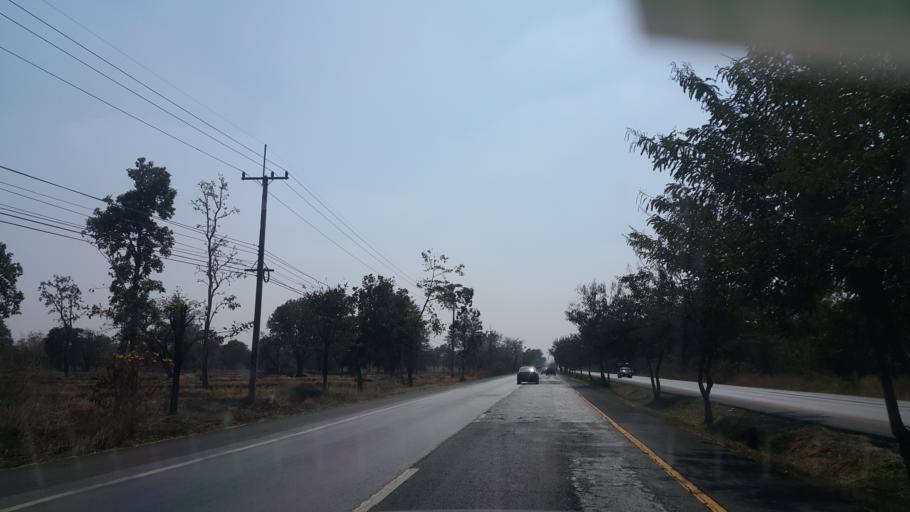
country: TH
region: Nakhon Ratchasima
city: Non Daeng
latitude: 15.3693
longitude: 102.4567
